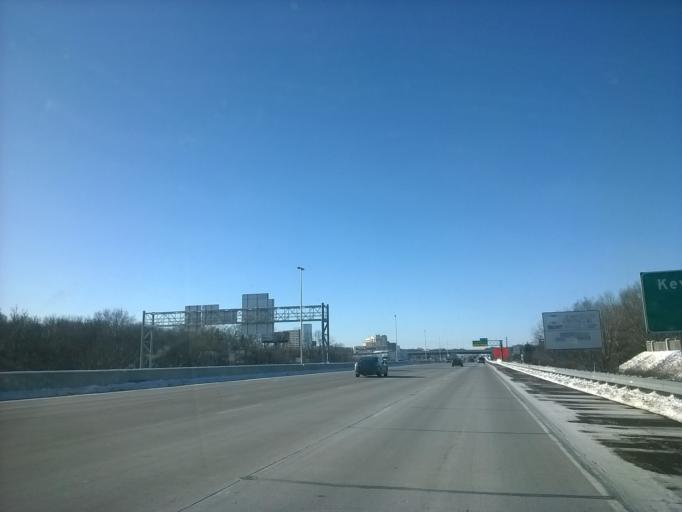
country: US
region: Indiana
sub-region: Hamilton County
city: Carmel
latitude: 39.9162
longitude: -86.0934
